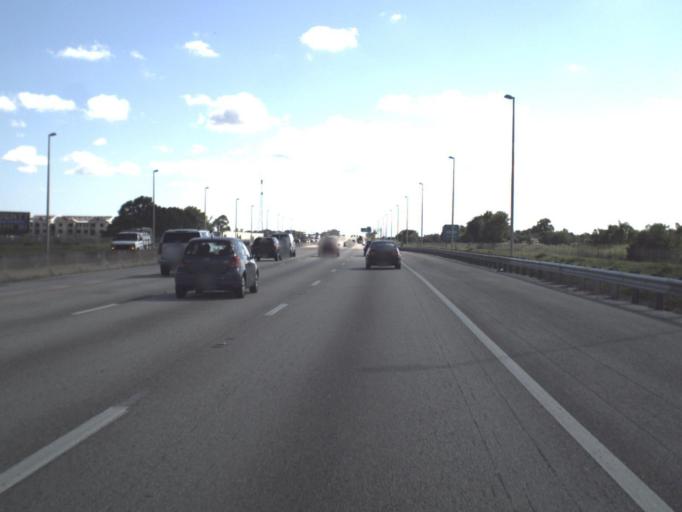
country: US
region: Florida
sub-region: Palm Beach County
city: Villages of Oriole
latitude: 26.4676
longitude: -80.1749
